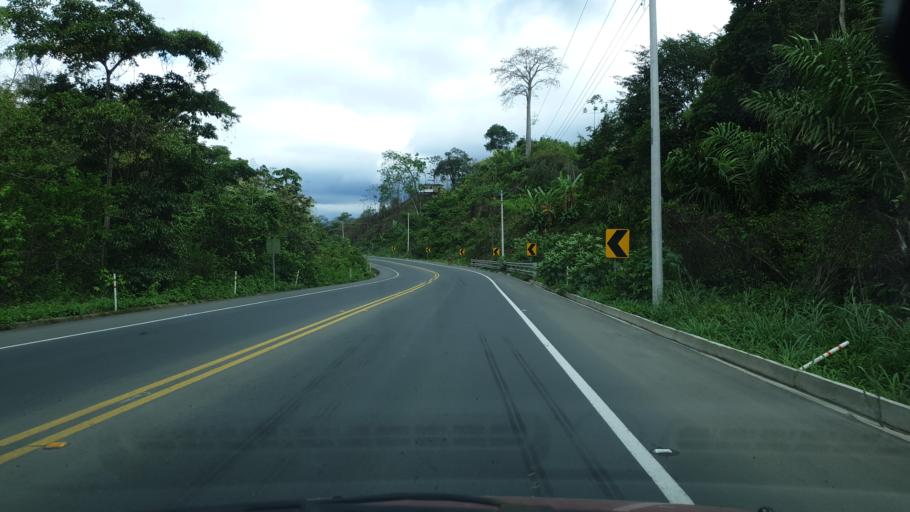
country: EC
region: Manabi
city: Pajan
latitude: -1.5638
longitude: -80.5230
